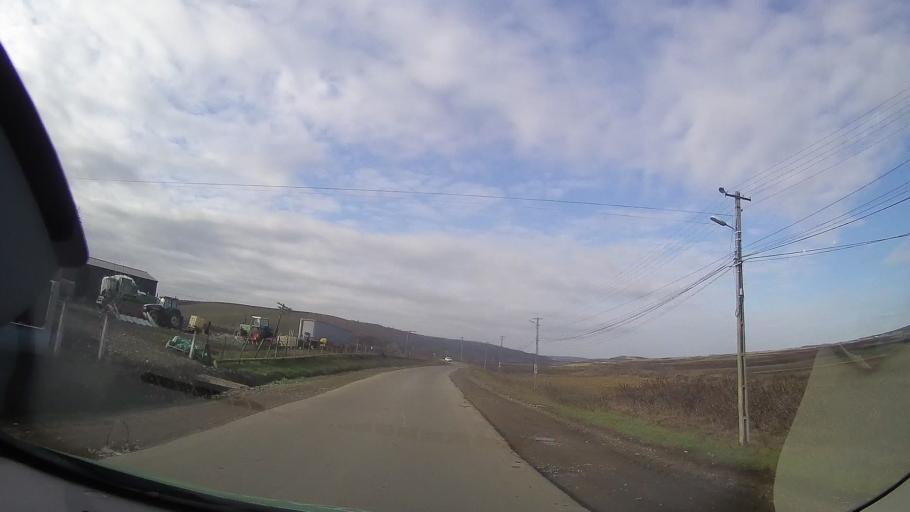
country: RO
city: Barza
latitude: 46.5479
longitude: 24.1263
